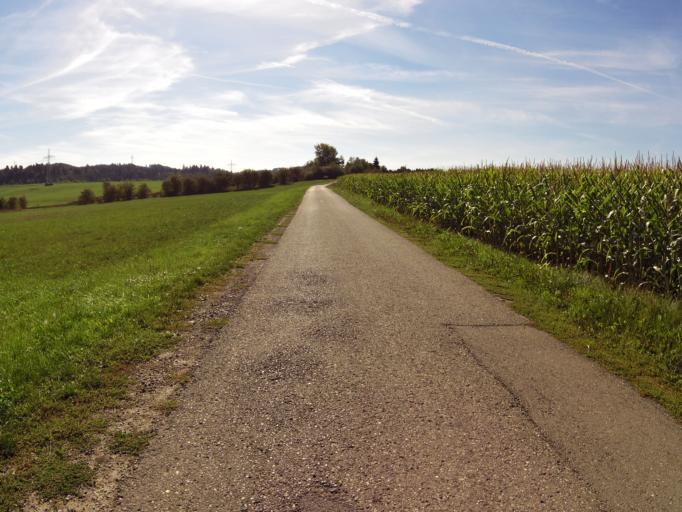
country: DE
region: Baden-Wuerttemberg
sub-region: Freiburg Region
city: Deisslingen
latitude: 48.0941
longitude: 8.5842
